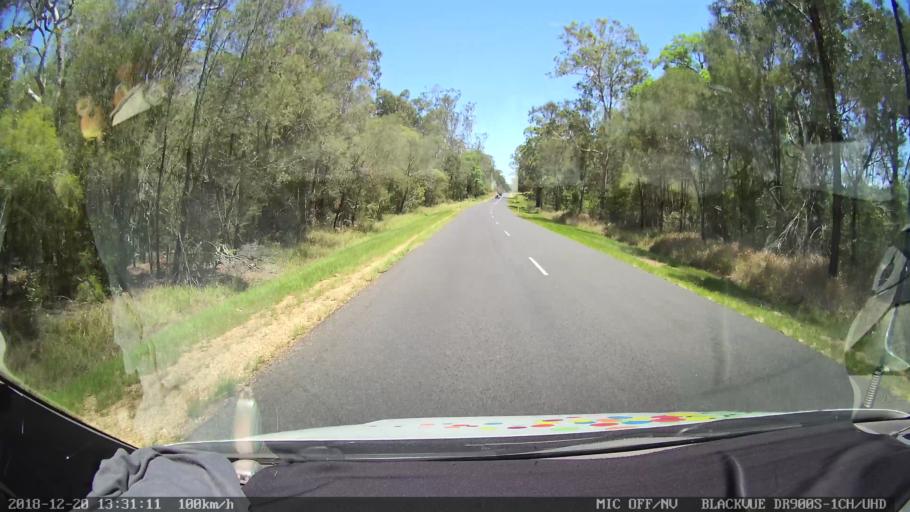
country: AU
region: New South Wales
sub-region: Clarence Valley
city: Gordon
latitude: -29.2141
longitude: 152.9899
